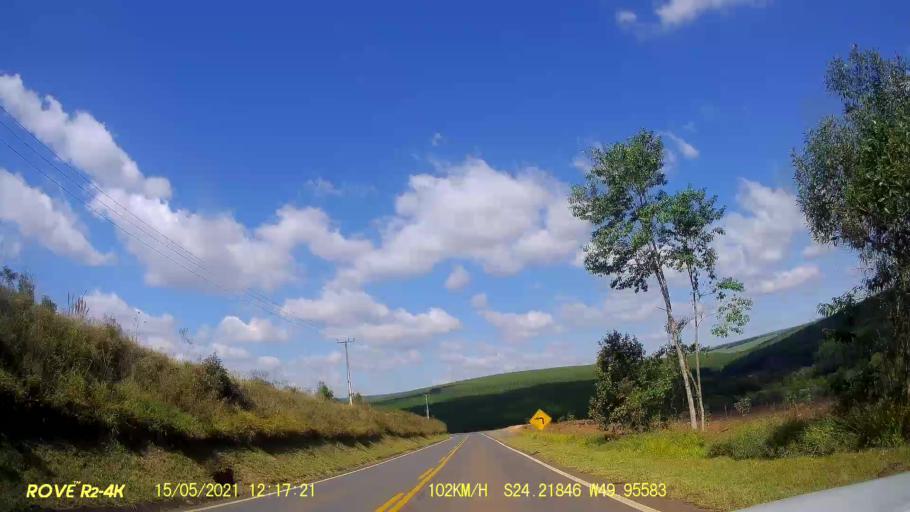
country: BR
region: Parana
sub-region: Jaguariaiva
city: Jaguariaiva
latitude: -24.2187
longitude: -49.9559
